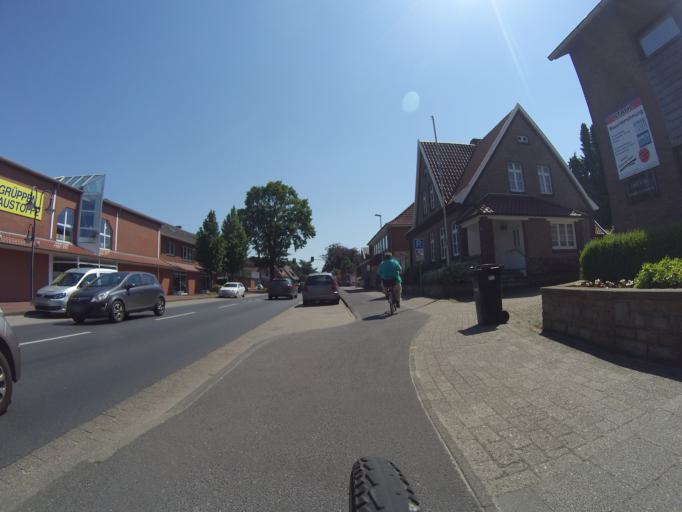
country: DE
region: Lower Saxony
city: Emlichheim
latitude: 52.6088
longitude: 6.8534
